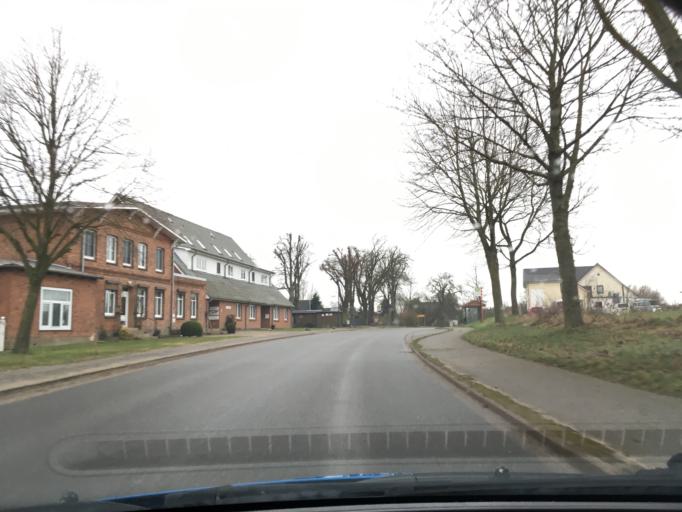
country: DE
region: Schleswig-Holstein
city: Woltersdorf
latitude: 53.5769
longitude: 10.6401
